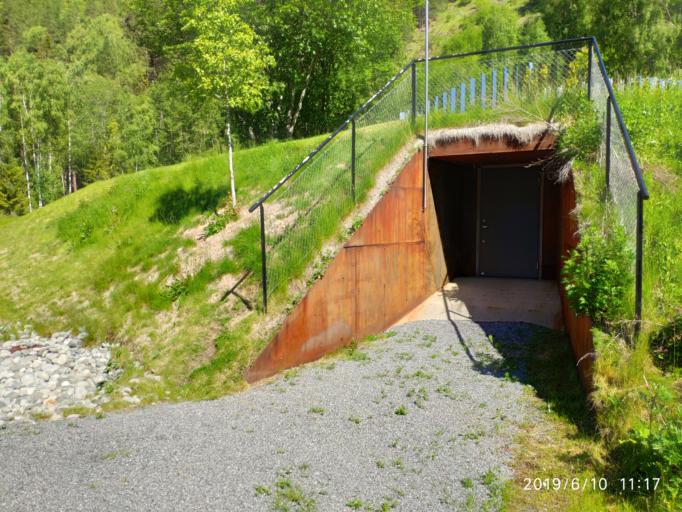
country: NO
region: Oppland
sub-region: Jevnaker
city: Jevnaker
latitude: 60.2224
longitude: 10.3682
